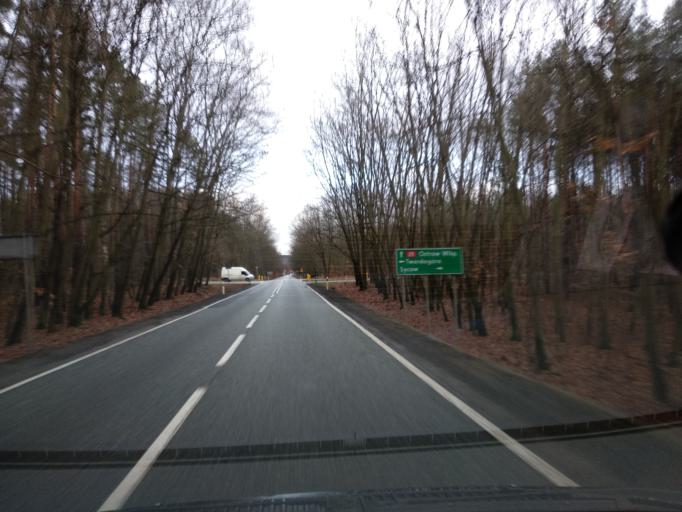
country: PL
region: Lower Silesian Voivodeship
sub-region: Powiat olesnicki
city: Miedzyborz
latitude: 51.3636
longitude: 17.6110
